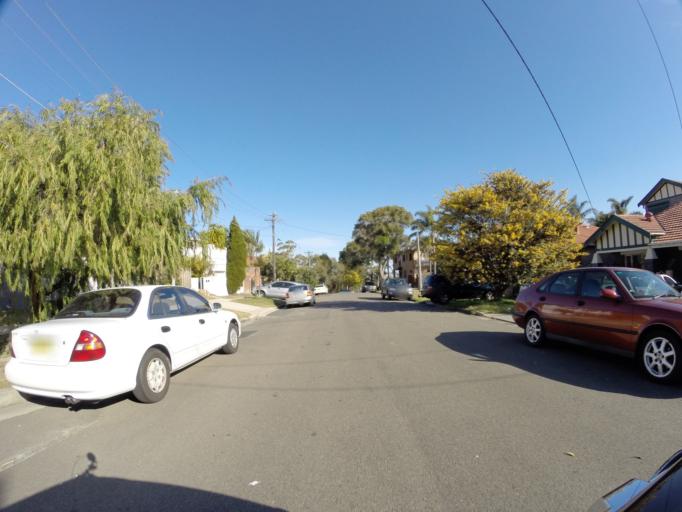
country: AU
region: New South Wales
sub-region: Randwick
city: Coogee
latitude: -33.9246
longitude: 151.2481
